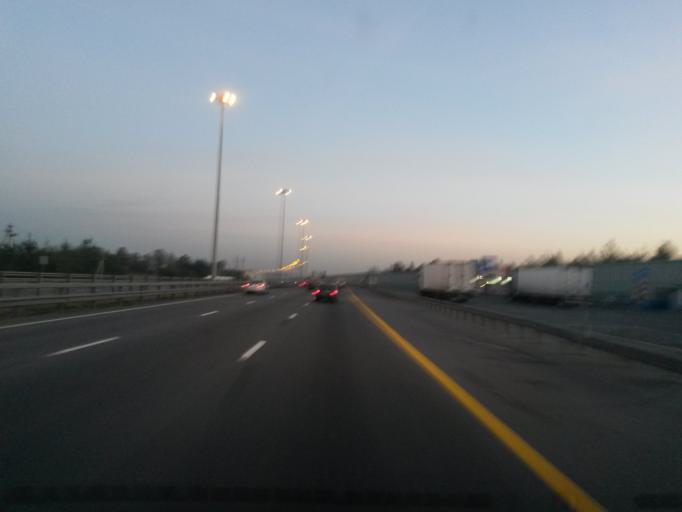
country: RU
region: Moskovskaya
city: Belyye Stolby
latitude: 55.3249
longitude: 37.8112
